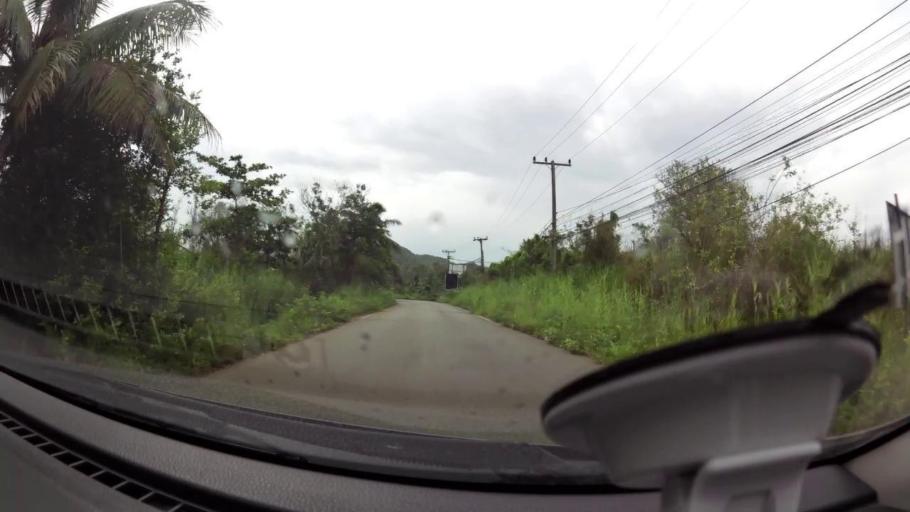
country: TH
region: Prachuap Khiri Khan
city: Pran Buri
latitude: 12.4462
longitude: 99.9668
